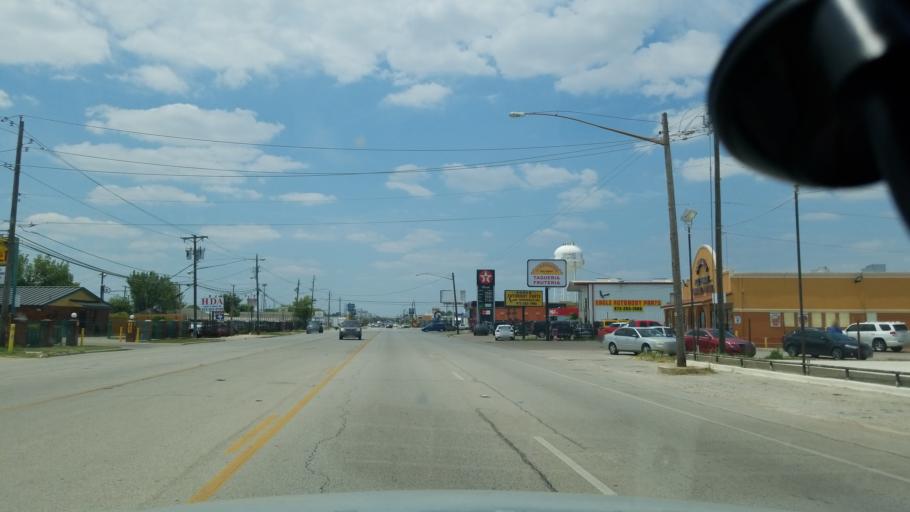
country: US
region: Texas
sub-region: Dallas County
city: Grand Prairie
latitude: 32.7481
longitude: -96.9825
